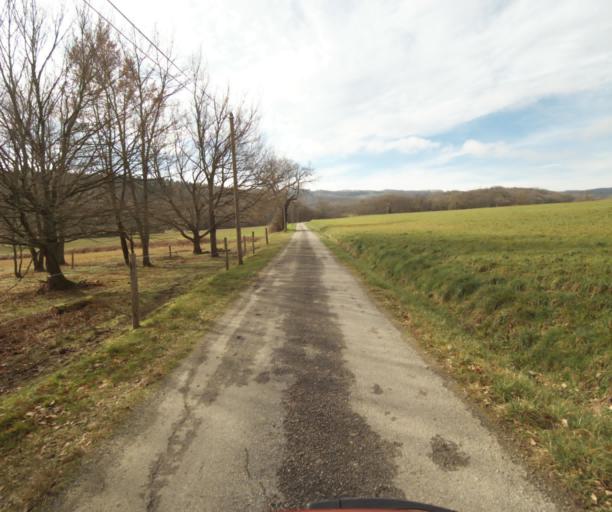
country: FR
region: Midi-Pyrenees
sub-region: Departement de l'Ariege
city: Pamiers
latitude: 43.1002
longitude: 1.5217
